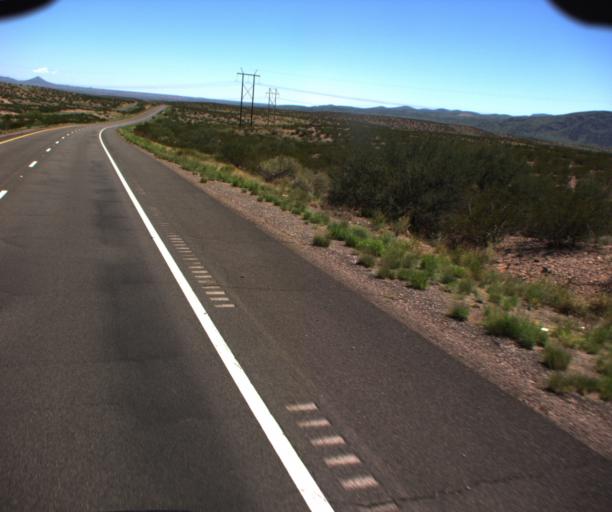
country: US
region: Arizona
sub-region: Greenlee County
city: Clifton
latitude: 32.9911
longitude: -109.2699
